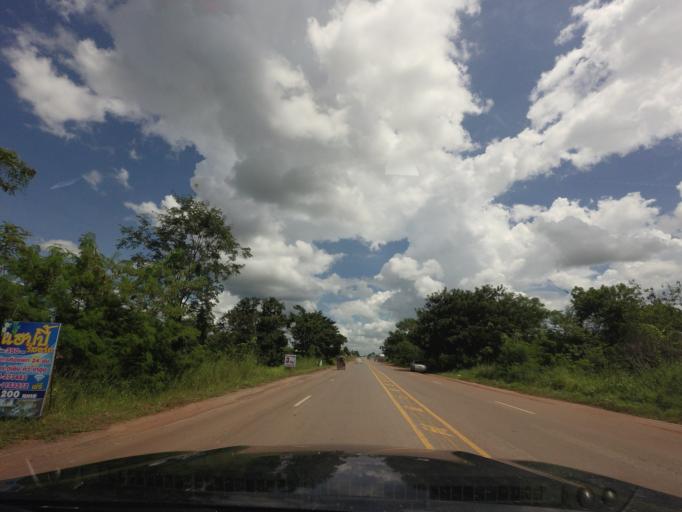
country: TH
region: Changwat Udon Thani
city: Ban Dung
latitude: 17.6804
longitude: 103.2317
